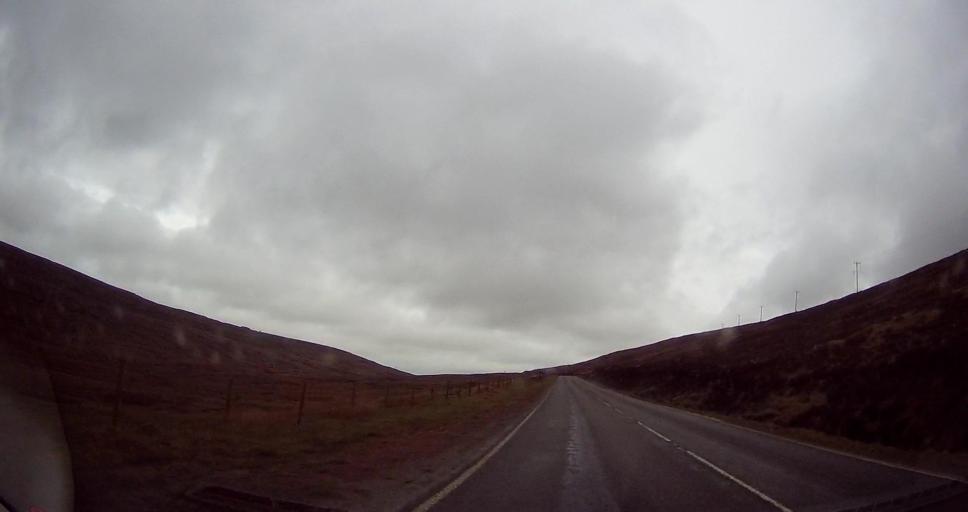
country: GB
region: Scotland
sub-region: Shetland Islands
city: Lerwick
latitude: 60.3179
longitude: -1.2471
